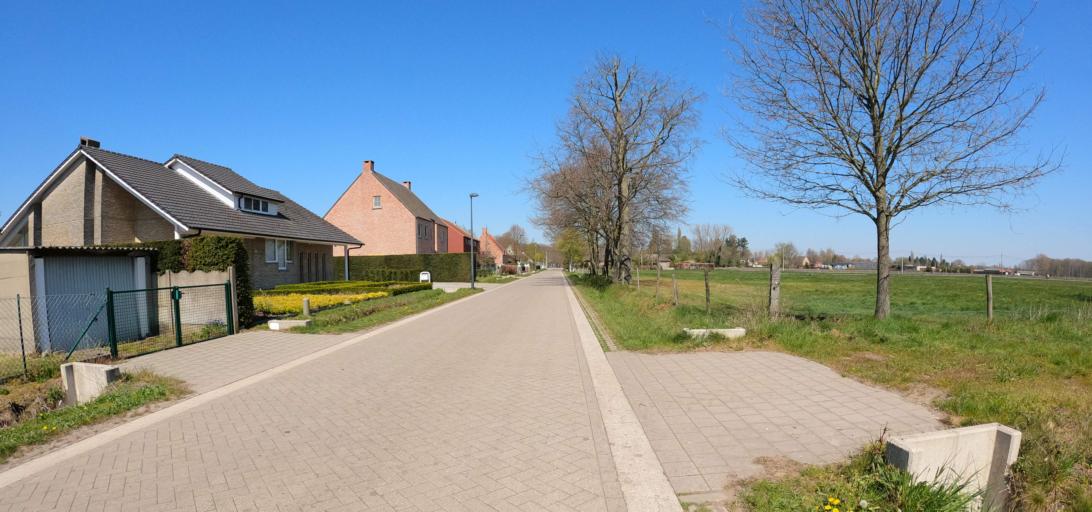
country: BE
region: Flanders
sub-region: Provincie Antwerpen
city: Oostmalle
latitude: 51.2982
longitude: 4.7501
